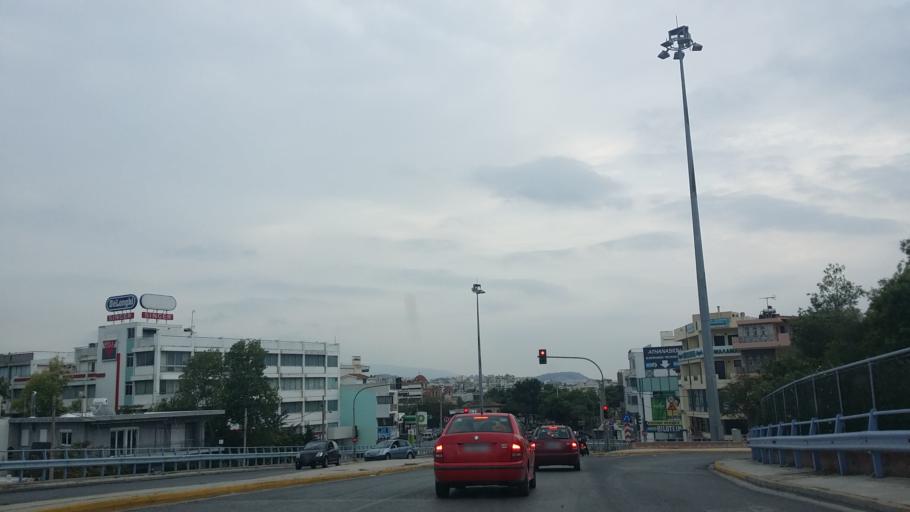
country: GR
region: Attica
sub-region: Nomarchia Athinas
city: Metamorfosi
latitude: 38.0683
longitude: 23.7599
